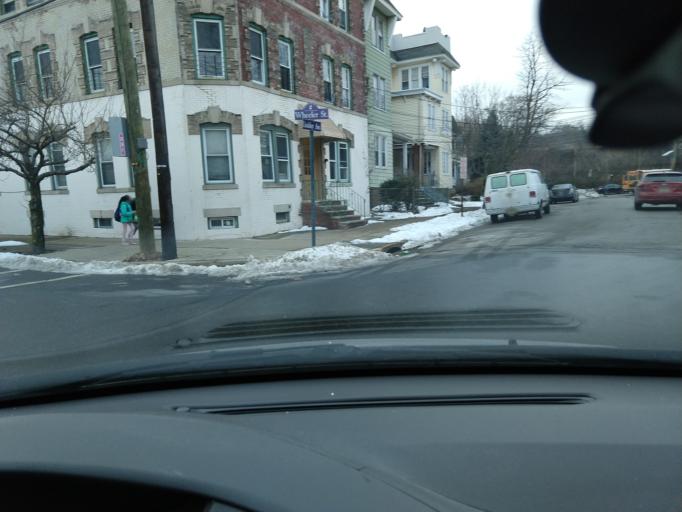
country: US
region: New Jersey
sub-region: Essex County
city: Orange
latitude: 40.7776
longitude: -74.2406
